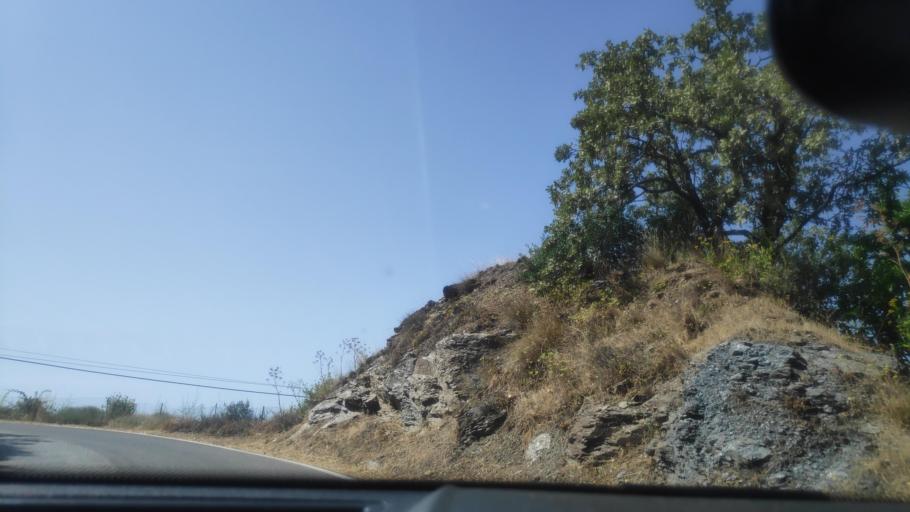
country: ES
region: Andalusia
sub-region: Provincia de Granada
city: Portugos
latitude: 36.9405
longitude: -3.3200
